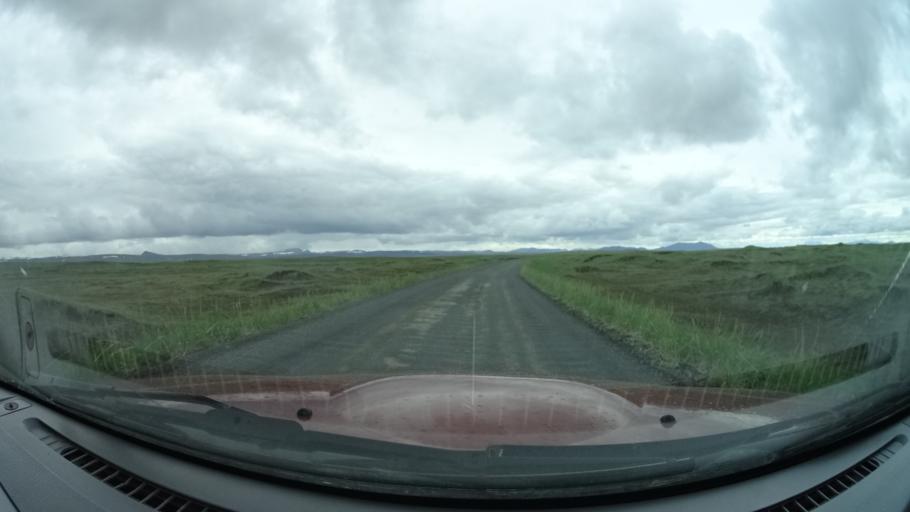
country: IS
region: Northeast
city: Laugar
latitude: 65.6929
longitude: -16.1888
